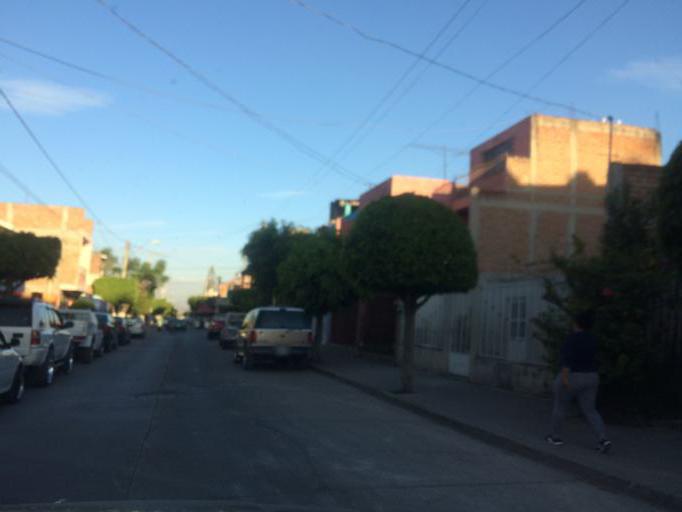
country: MX
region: Guanajuato
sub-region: Leon
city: La Ermita
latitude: 21.1372
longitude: -101.7113
